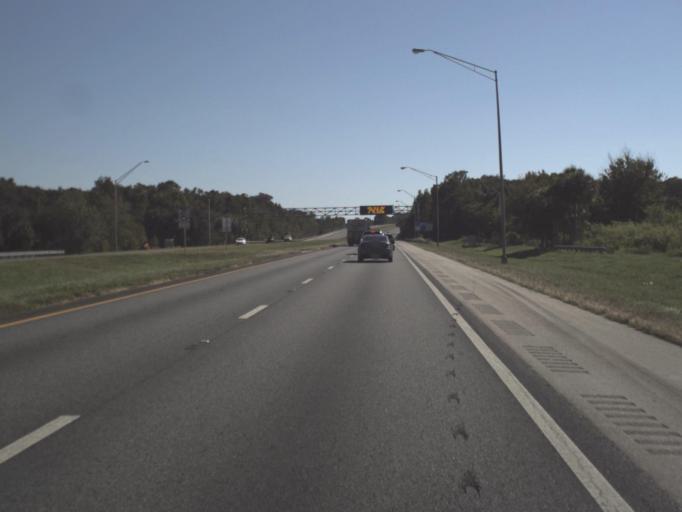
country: US
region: Florida
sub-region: Seminole County
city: Oviedo
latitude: 28.7006
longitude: -81.2330
